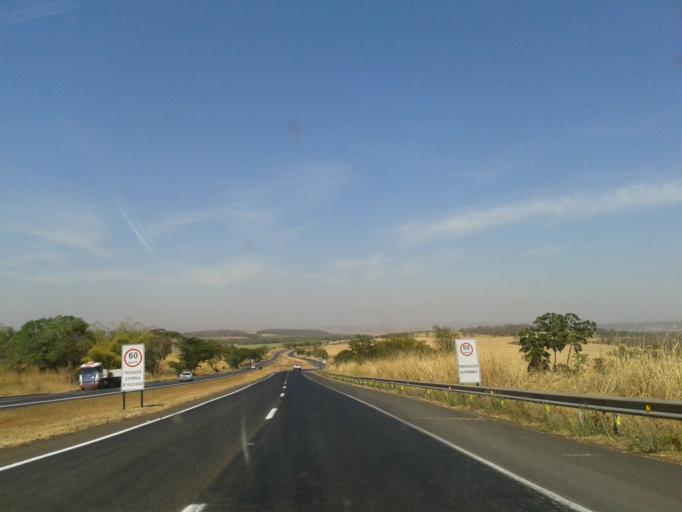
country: BR
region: Goias
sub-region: Goiatuba
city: Goiatuba
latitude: -18.0772
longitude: -49.2710
